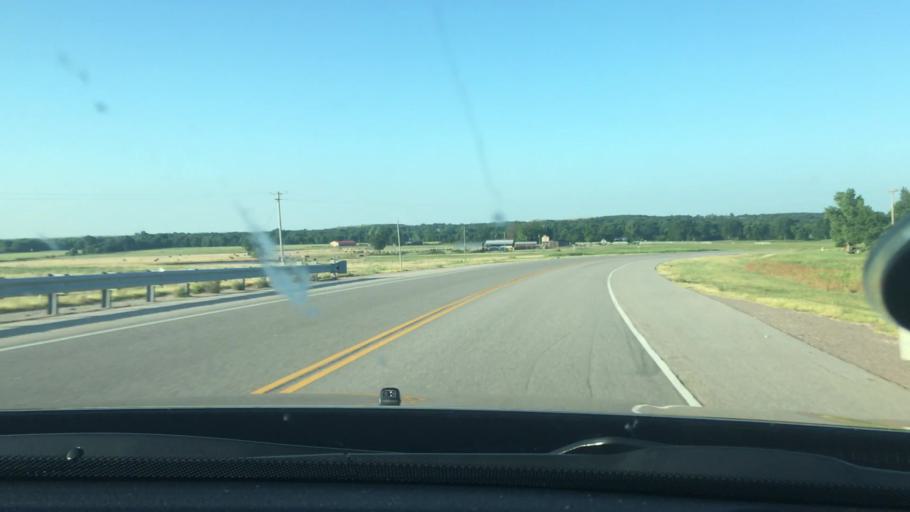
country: US
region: Oklahoma
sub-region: Pontotoc County
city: Ada
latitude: 34.6518
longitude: -96.7956
